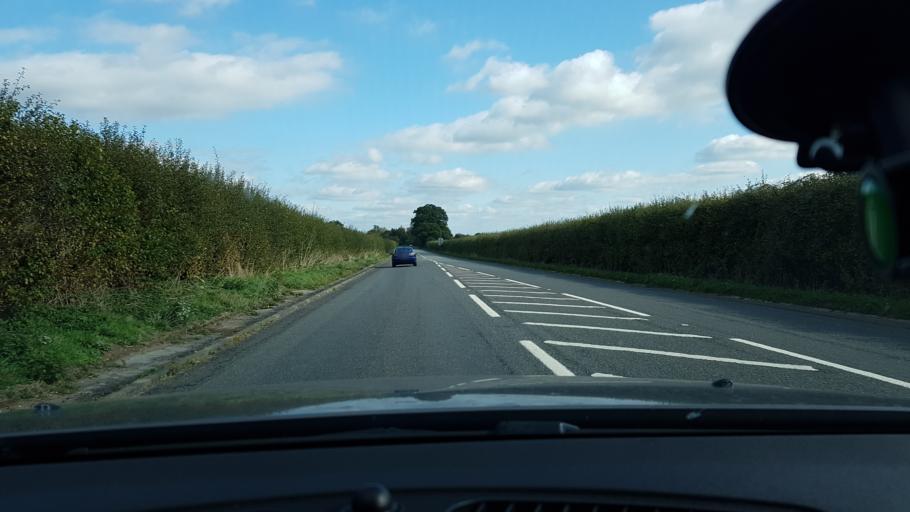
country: GB
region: England
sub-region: West Berkshire
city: Kintbury
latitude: 51.4138
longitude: -1.4650
